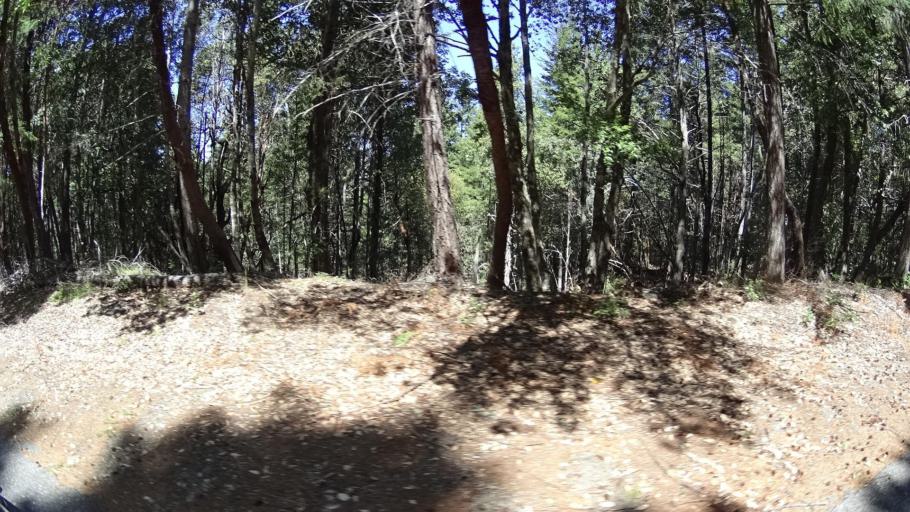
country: US
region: California
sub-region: Humboldt County
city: Rio Dell
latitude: 40.2632
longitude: -124.1082
